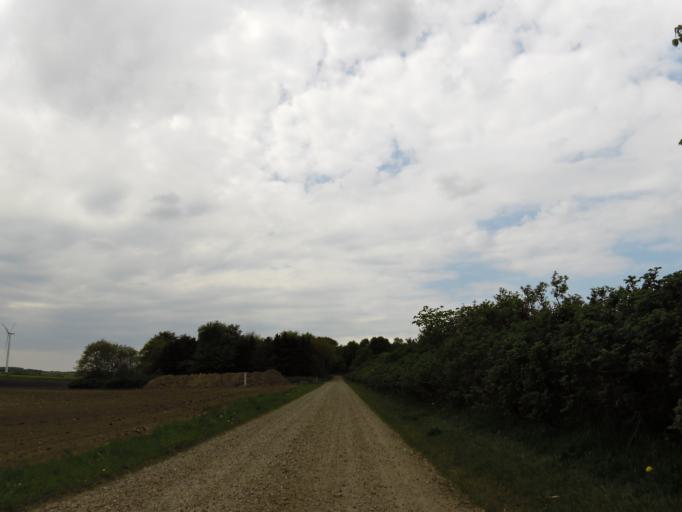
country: DK
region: Central Jutland
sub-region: Holstebro Kommune
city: Vinderup
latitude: 56.5168
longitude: 8.8000
